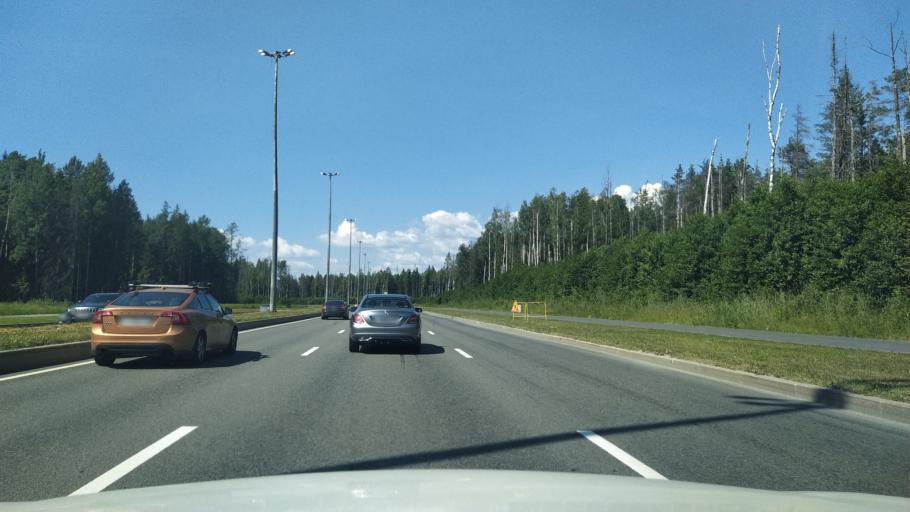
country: RU
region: St.-Petersburg
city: Levashovo
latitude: 60.0602
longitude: 30.2184
